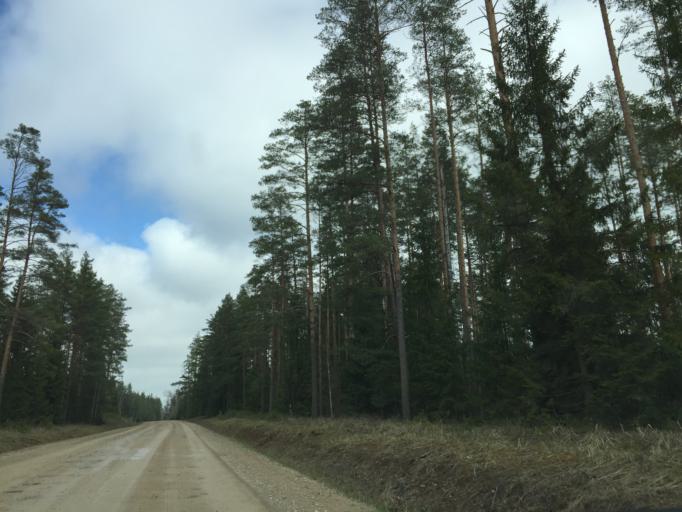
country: EE
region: Valgamaa
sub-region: Valga linn
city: Valga
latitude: 57.6159
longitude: 26.2357
